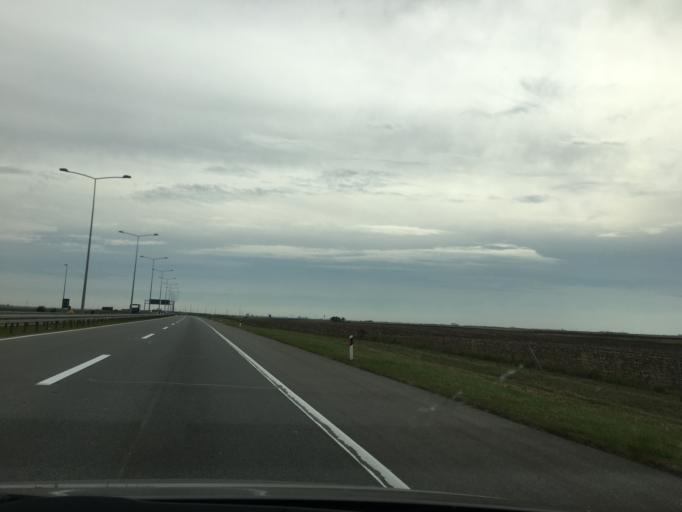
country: RS
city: Krcedin
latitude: 45.1002
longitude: 20.1135
